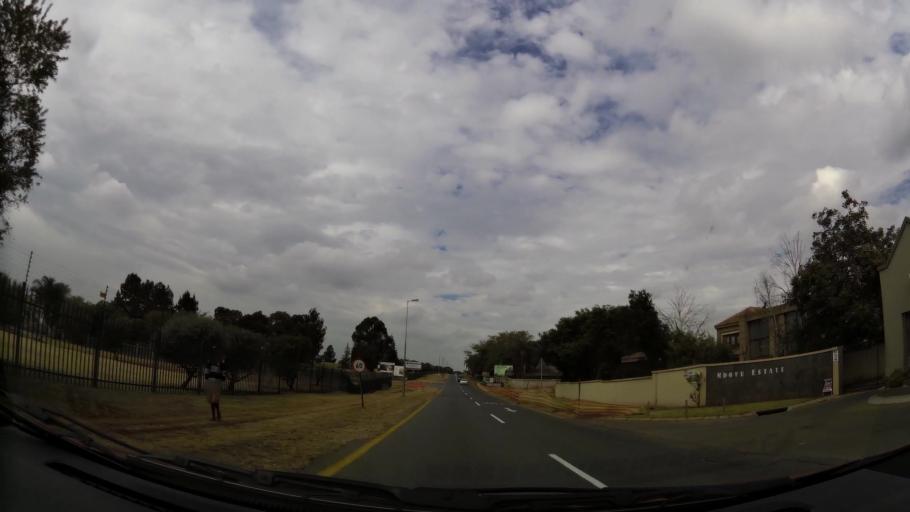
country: ZA
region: Gauteng
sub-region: West Rand District Municipality
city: Muldersdriseloop
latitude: -26.0778
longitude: 27.8610
